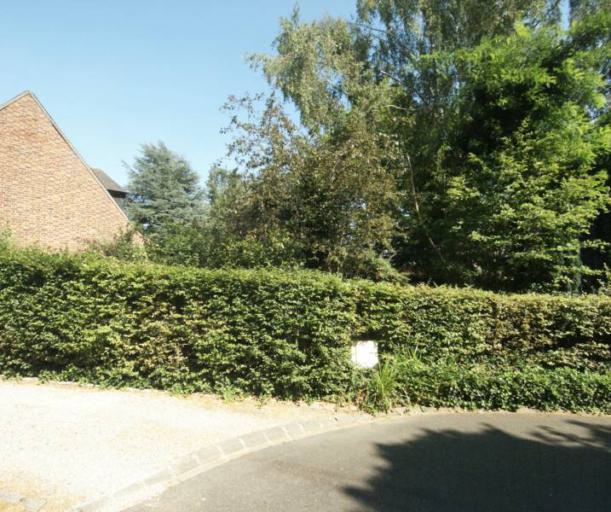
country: FR
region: Nord-Pas-de-Calais
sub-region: Departement du Nord
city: Bondues
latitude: 50.7037
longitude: 3.0788
